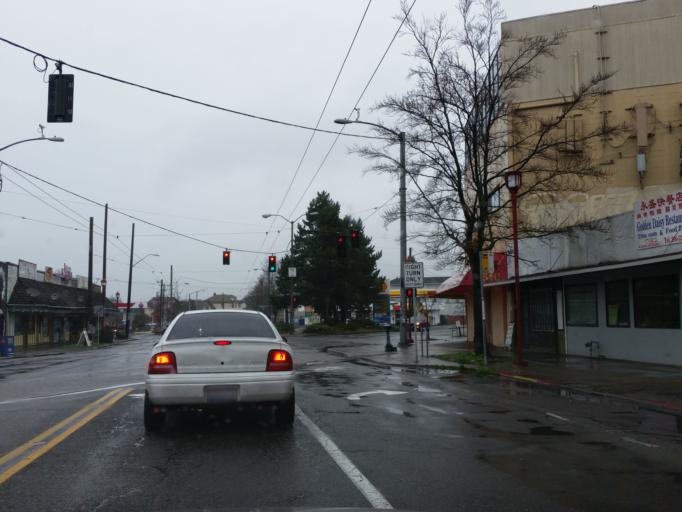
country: US
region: Washington
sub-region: King County
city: Seattle
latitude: 47.5804
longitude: -122.3132
